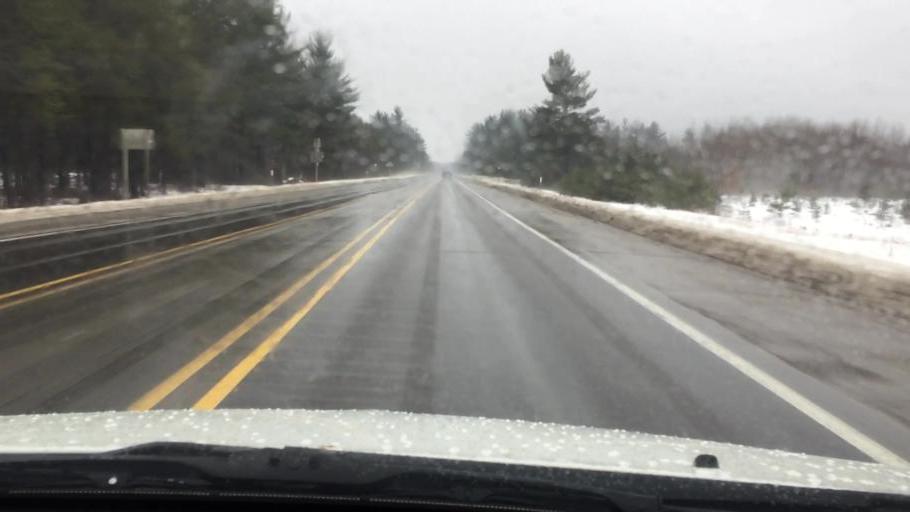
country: US
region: Michigan
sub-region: Kalkaska County
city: Kalkaska
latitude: 44.7155
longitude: -85.1911
